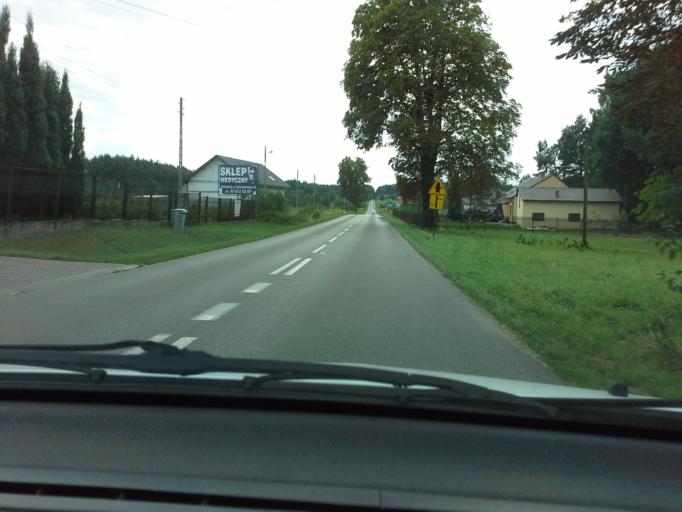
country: PL
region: Lesser Poland Voivodeship
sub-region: Powiat chrzanowski
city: Bolecin
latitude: 50.1209
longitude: 19.4628
